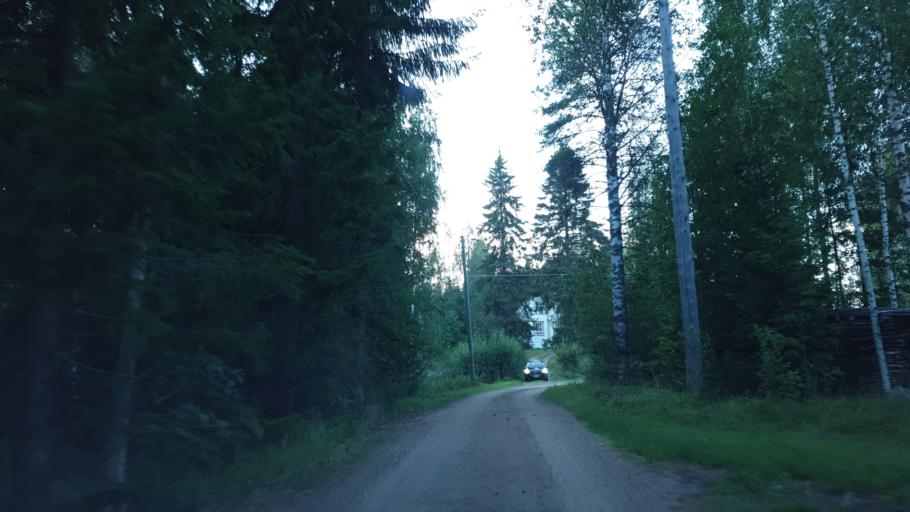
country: FI
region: Northern Savo
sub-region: Koillis-Savo
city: Kaavi
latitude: 62.9769
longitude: 28.7814
